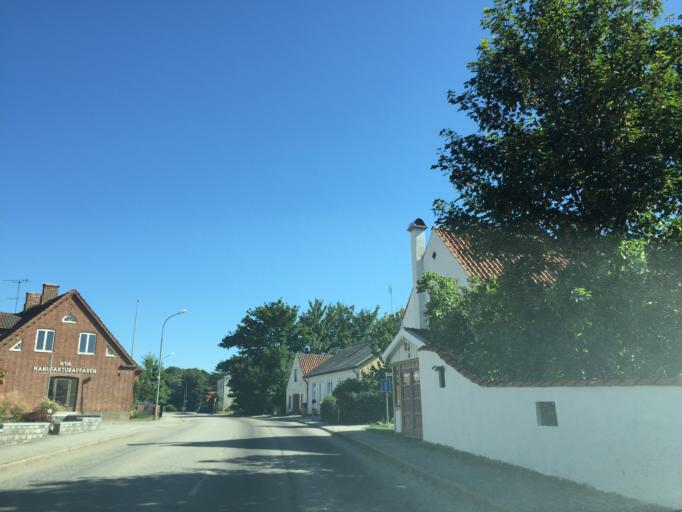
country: SE
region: Skane
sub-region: Ystads Kommun
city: Kopingebro
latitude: 55.4404
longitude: 14.1129
